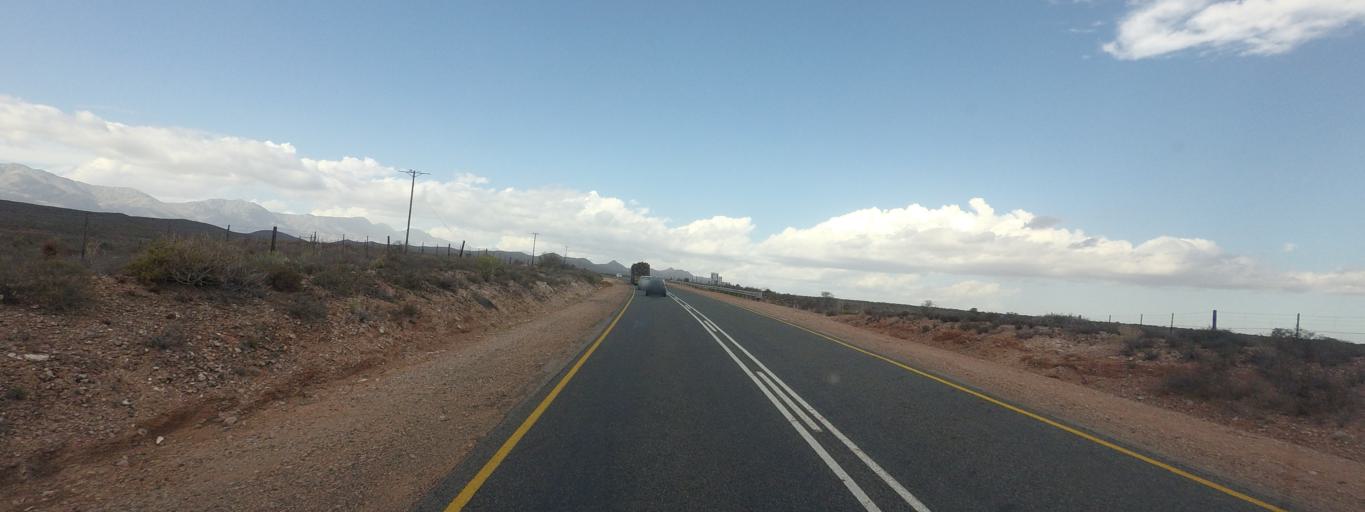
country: ZA
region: Western Cape
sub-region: Central Karoo District Municipality
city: Prince Albert
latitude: -33.5315
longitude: 21.7124
